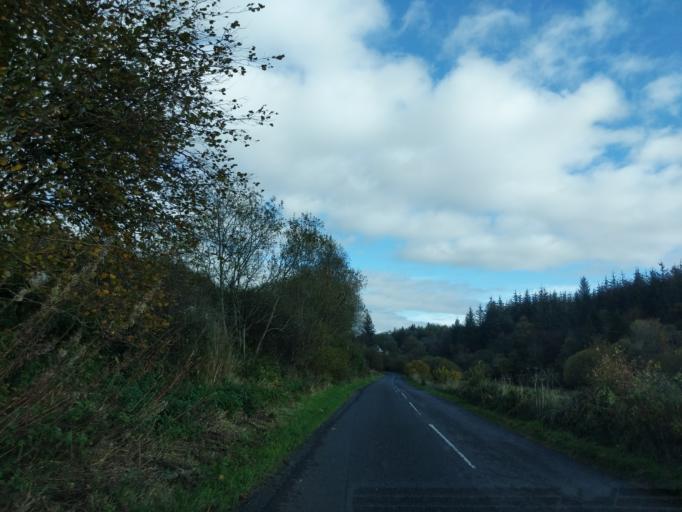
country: GB
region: Scotland
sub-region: Dumfries and Galloway
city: Sanquhar
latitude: 55.1728
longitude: -3.9526
